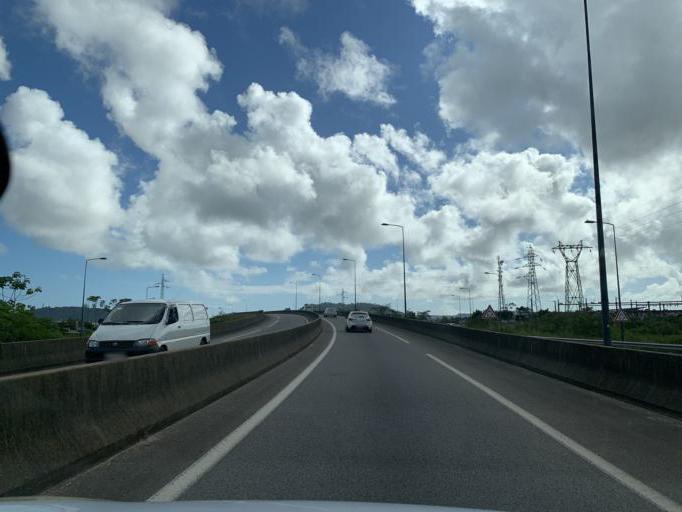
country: GF
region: Guyane
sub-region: Guyane
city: Cayenne
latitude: 4.8909
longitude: -52.3354
